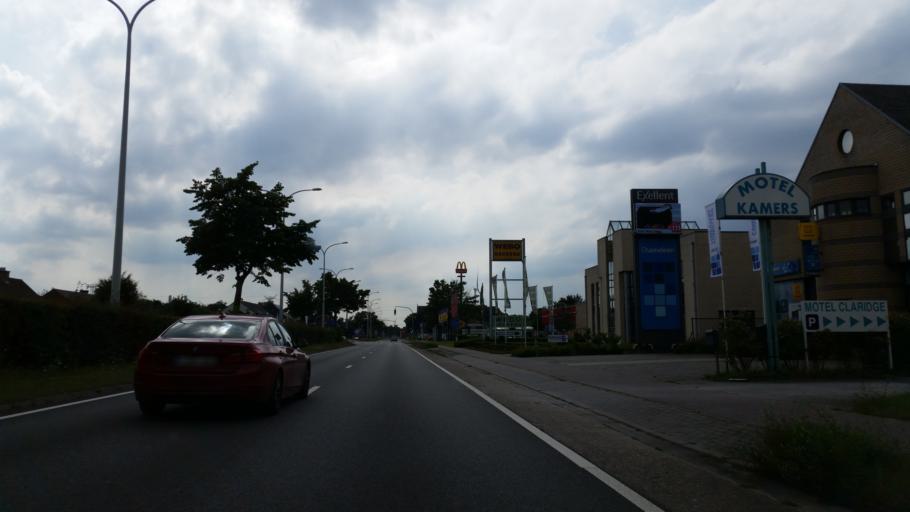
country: BE
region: Flanders
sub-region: Provincie Antwerpen
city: Geel
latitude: 51.1440
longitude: 4.9515
